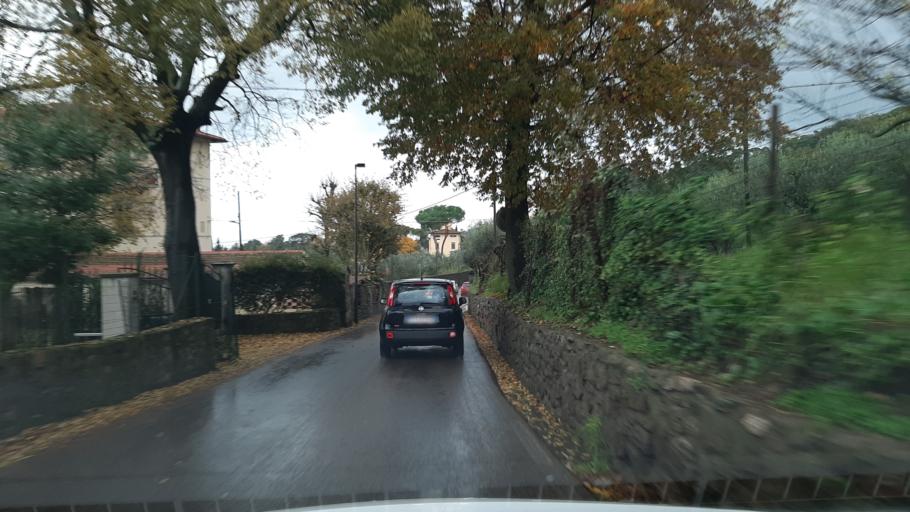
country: IT
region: Tuscany
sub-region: Province of Florence
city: Florence
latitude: 43.8088
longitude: 11.2604
